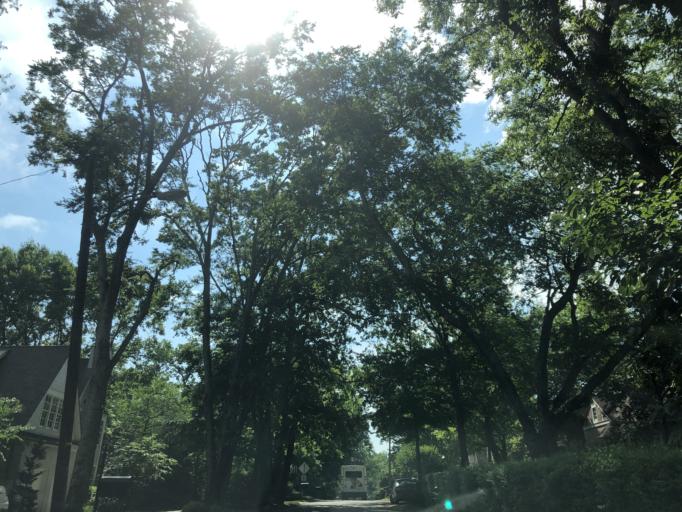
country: US
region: Tennessee
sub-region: Davidson County
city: Belle Meade
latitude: 36.1251
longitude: -86.8234
